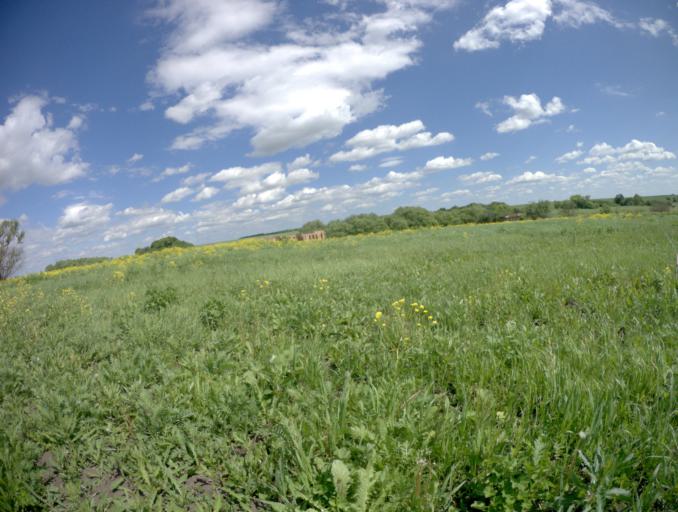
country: RU
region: Ivanovo
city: Gavrilov Posad
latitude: 56.4410
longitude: 40.2475
